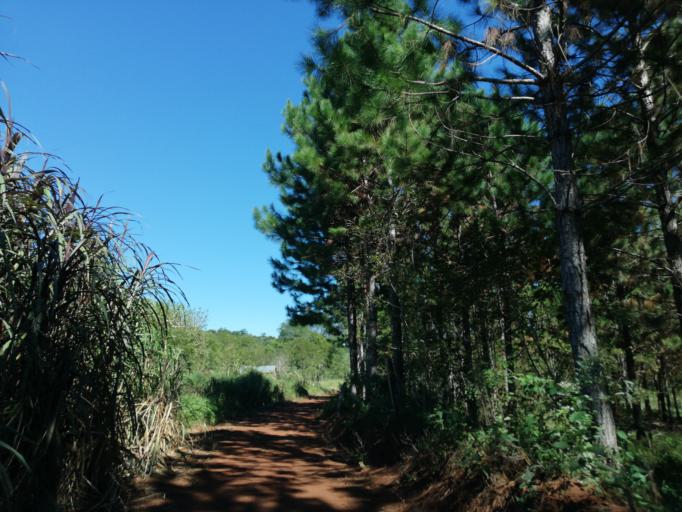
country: AR
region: Misiones
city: El Soberbio
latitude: -27.0637
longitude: -54.3779
